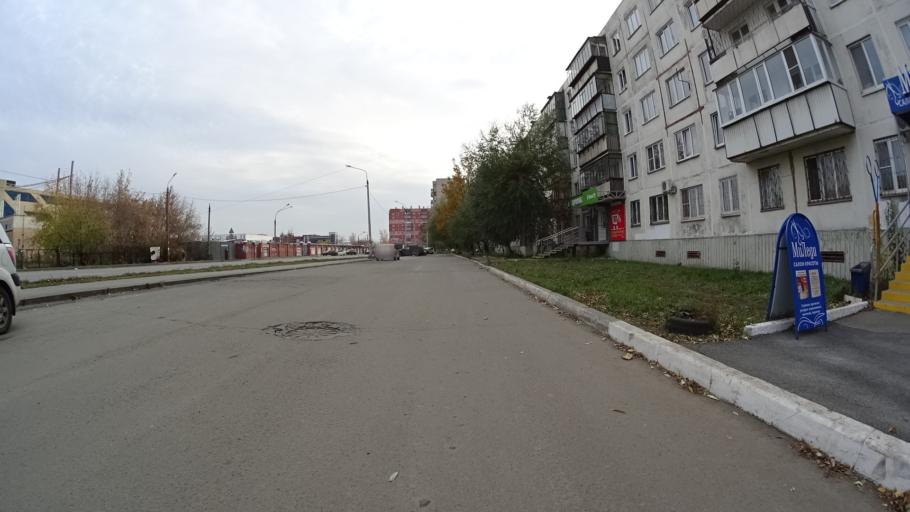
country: RU
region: Chelyabinsk
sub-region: Gorod Chelyabinsk
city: Chelyabinsk
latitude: 55.1911
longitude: 61.3177
